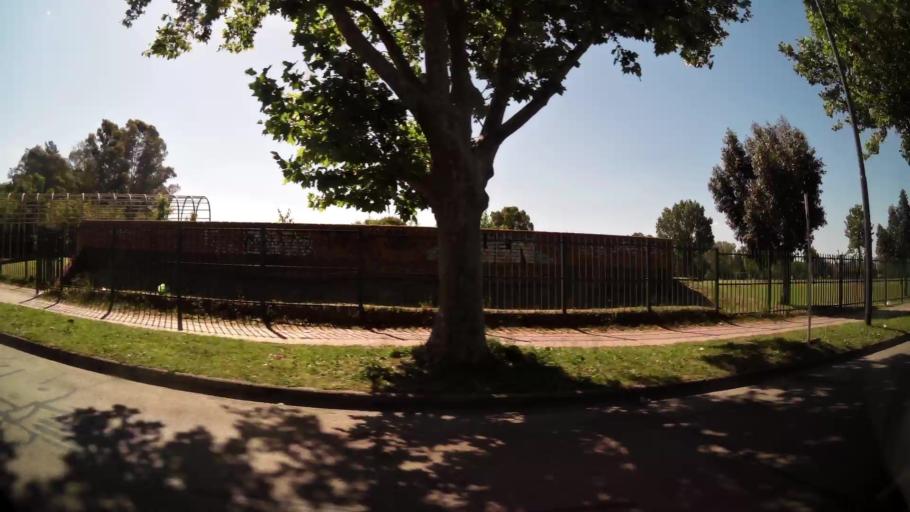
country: AR
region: Buenos Aires F.D.
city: Villa Lugano
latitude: -34.6850
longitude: -58.4561
